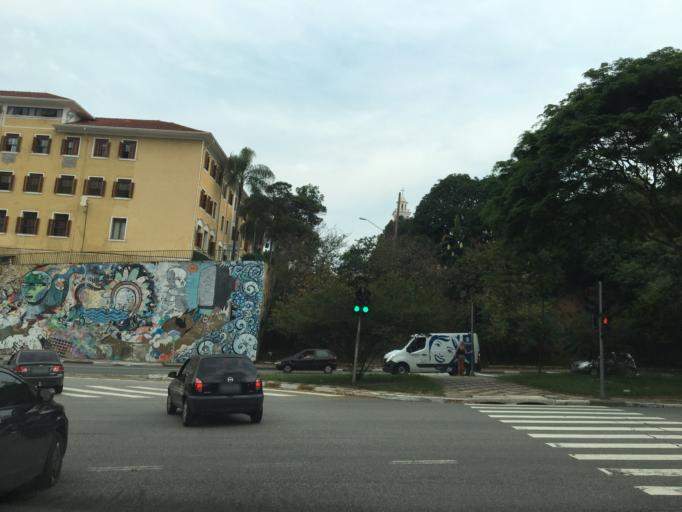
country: BR
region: Sao Paulo
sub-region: Sao Paulo
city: Sao Paulo
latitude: -23.5557
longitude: -46.6827
